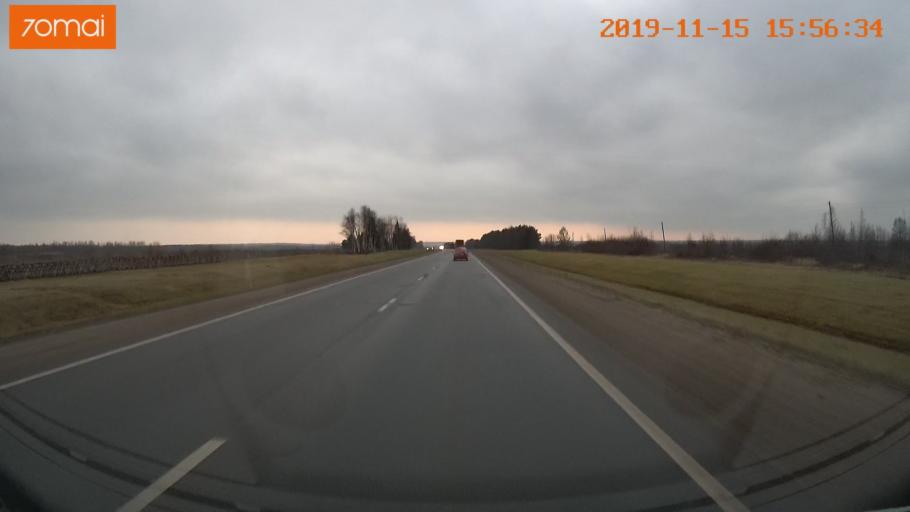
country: RU
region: Jaroslavl
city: Yaroslavl
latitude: 57.8407
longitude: 39.9723
